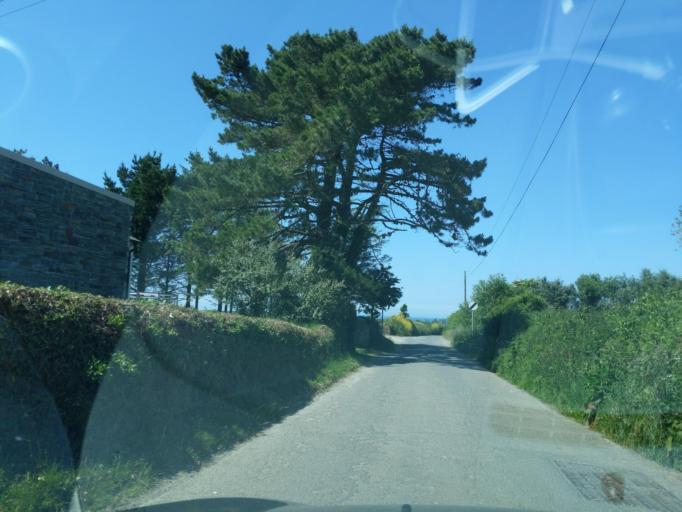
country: GB
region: England
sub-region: Cornwall
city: Wadebridge
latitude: 50.5736
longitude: -4.8294
